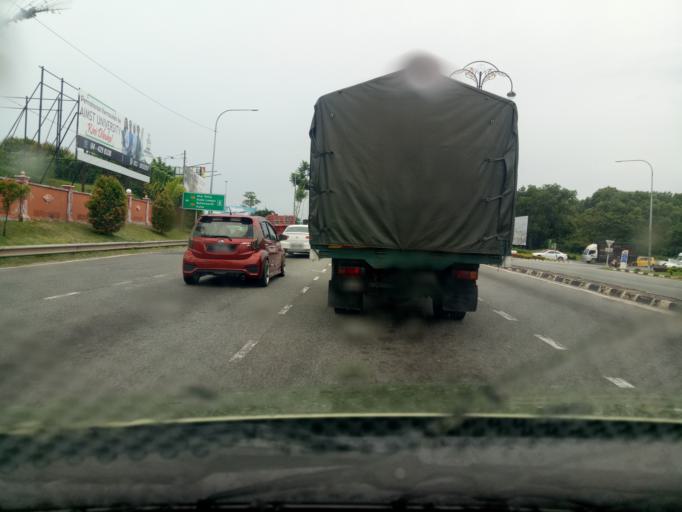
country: MY
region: Kedah
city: Sungai Petani
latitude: 5.6777
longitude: 100.5081
